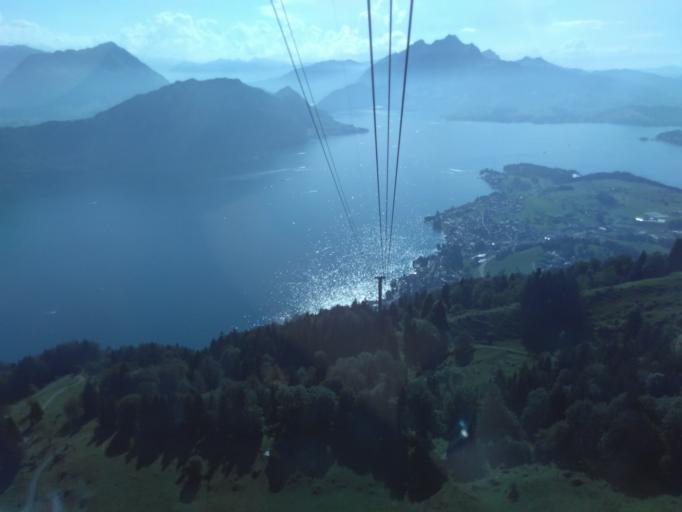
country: CH
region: Lucerne
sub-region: Lucerne-Land District
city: Weggis
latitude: 47.0401
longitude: 8.4564
